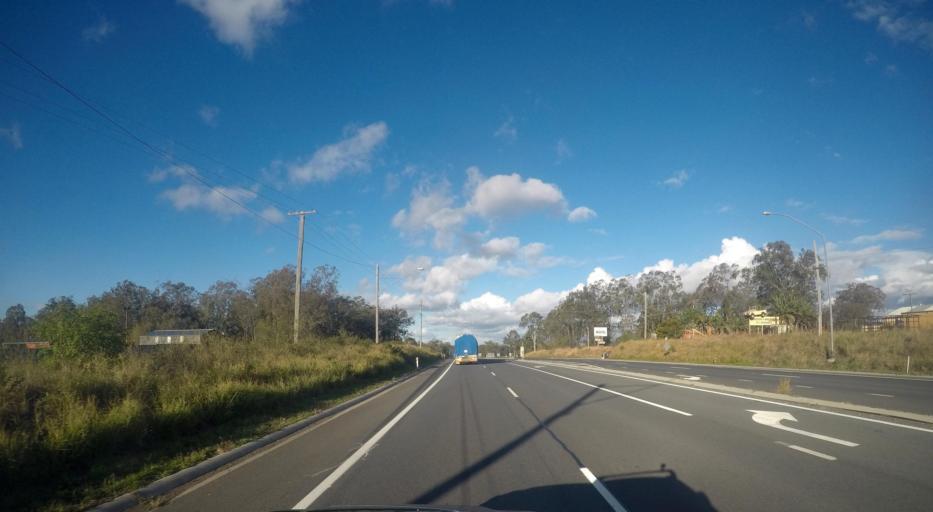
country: AU
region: Queensland
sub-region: Toowoomba
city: Rangeville
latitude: -27.5489
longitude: 152.1076
